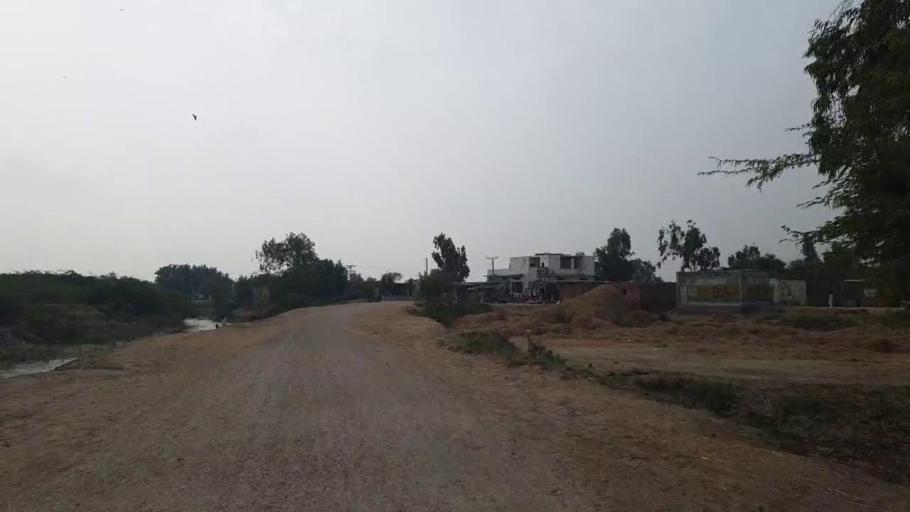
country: PK
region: Sindh
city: Kario
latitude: 24.8822
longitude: 68.5257
